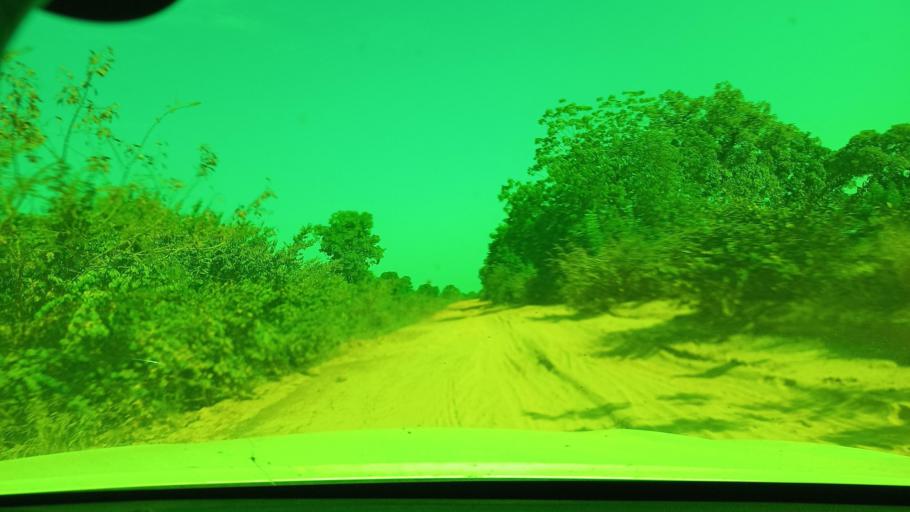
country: ML
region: Bamako
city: Bamako
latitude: 12.3964
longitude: -7.9798
